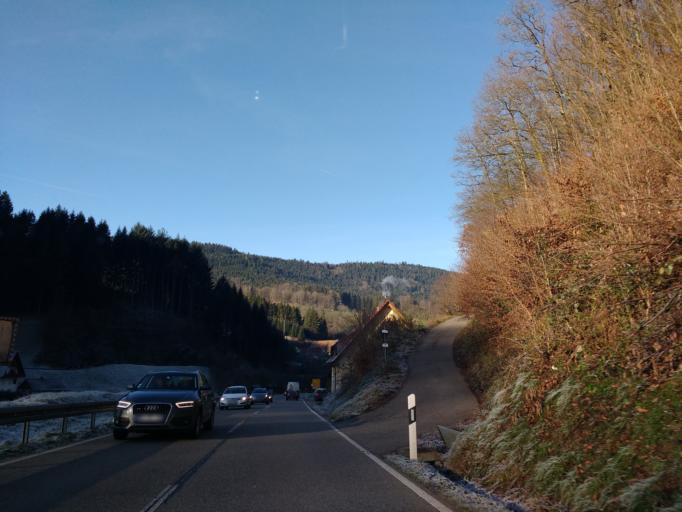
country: DE
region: Baden-Wuerttemberg
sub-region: Freiburg Region
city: Bad Peterstal-Griesbach
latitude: 48.4297
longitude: 8.1796
